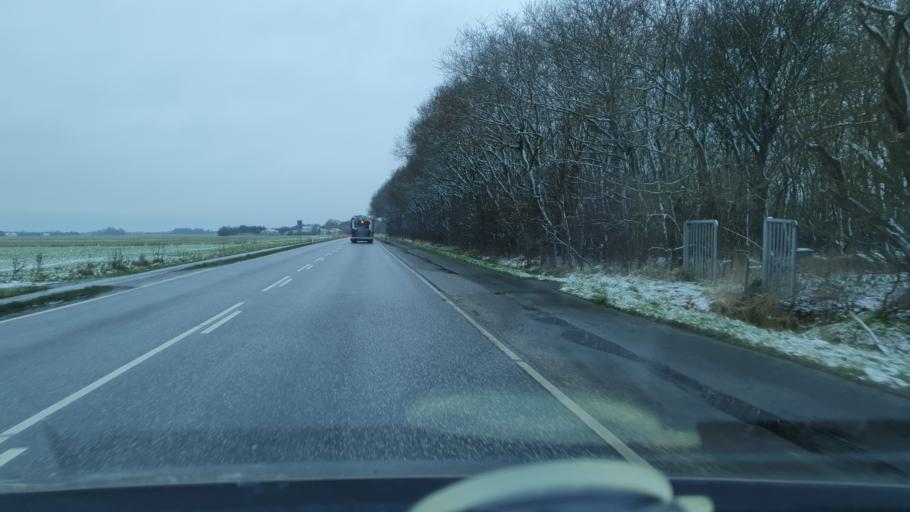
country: DK
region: North Denmark
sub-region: Jammerbugt Kommune
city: Brovst
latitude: 57.1203
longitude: 9.6177
